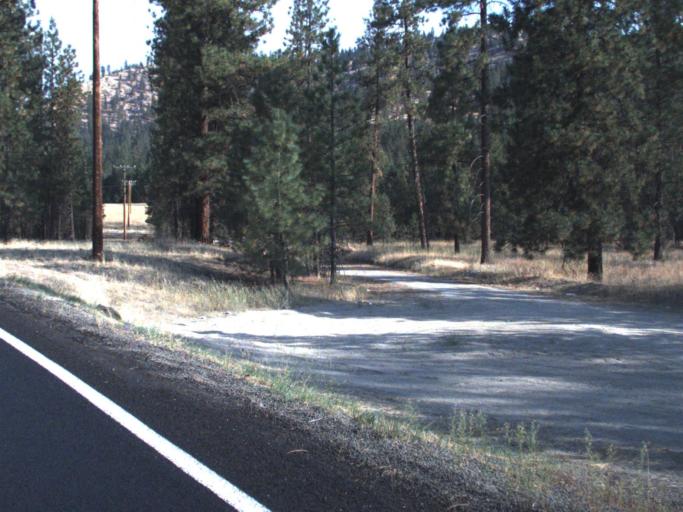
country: US
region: Washington
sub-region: Spokane County
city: Deer Park
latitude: 47.8695
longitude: -117.6479
